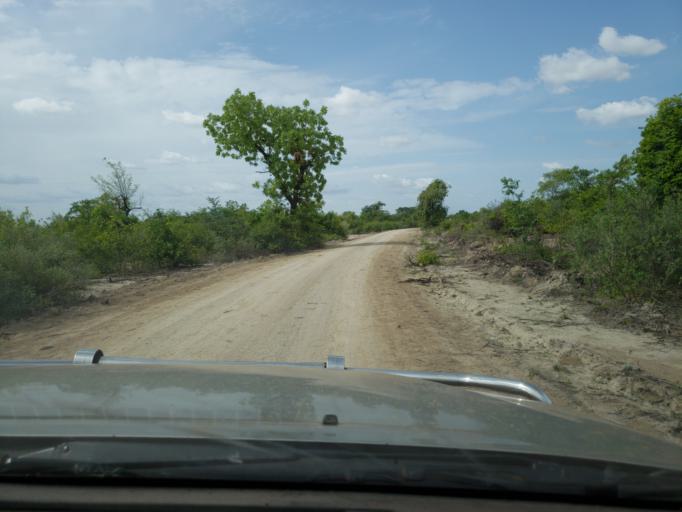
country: ML
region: Segou
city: Bla
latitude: 12.7664
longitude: -5.6207
